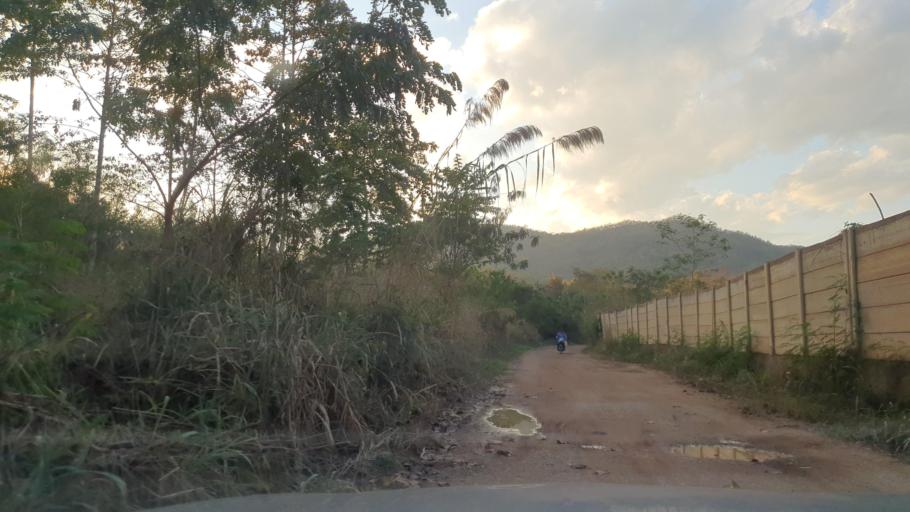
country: TH
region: Chiang Mai
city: Hang Dong
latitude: 18.7347
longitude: 98.8838
